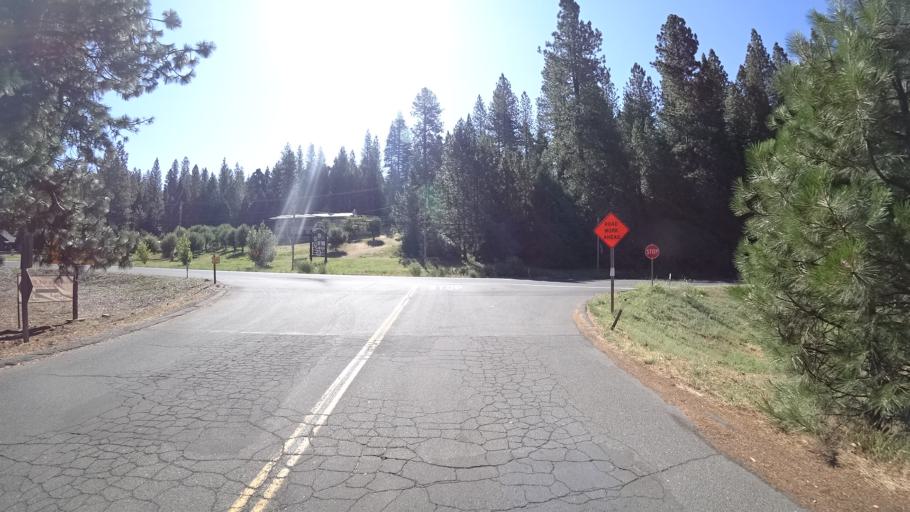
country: US
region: California
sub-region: Calaveras County
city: Arnold
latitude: 38.2408
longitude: -120.3624
